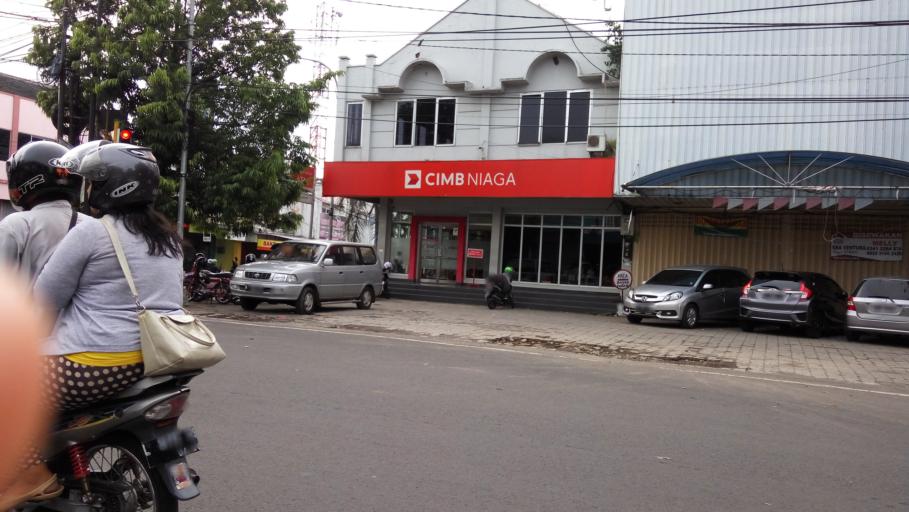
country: ID
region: East Java
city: Malang
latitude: -7.9670
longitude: 112.6137
